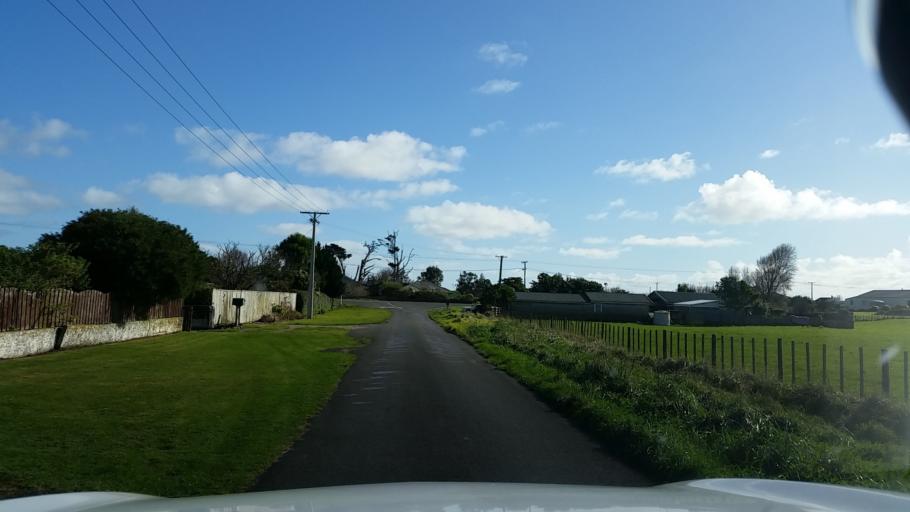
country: NZ
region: Taranaki
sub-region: South Taranaki District
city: Patea
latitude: -39.7117
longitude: 174.4501
